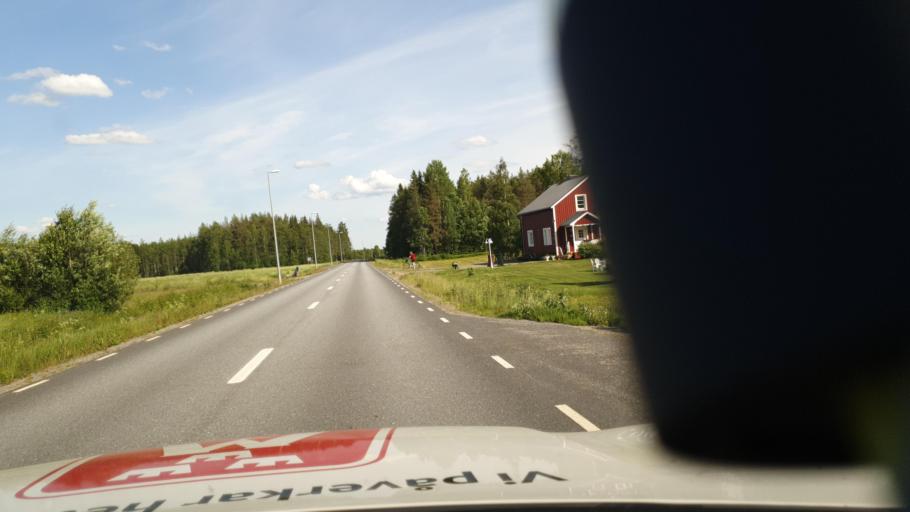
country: SE
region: Vaesterbotten
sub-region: Skelleftea Kommun
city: Forsbacka
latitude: 64.6952
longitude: 20.4881
